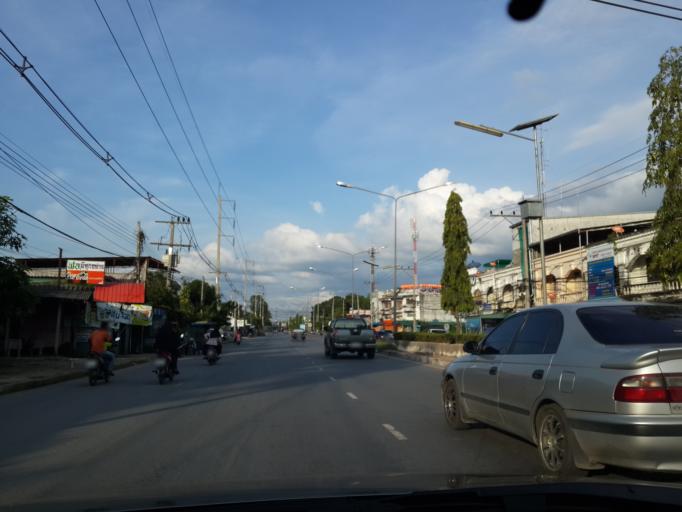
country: TH
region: Yala
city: Yala
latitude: 6.5433
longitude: 101.2710
